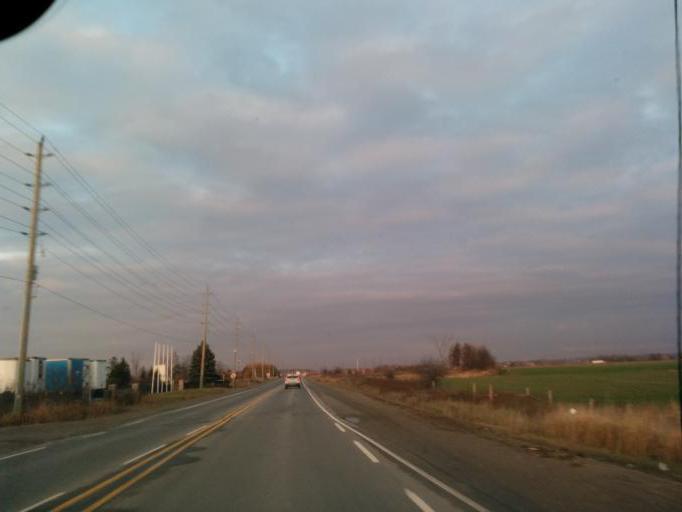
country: CA
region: Ontario
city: Brampton
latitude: 43.8402
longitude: -79.7041
